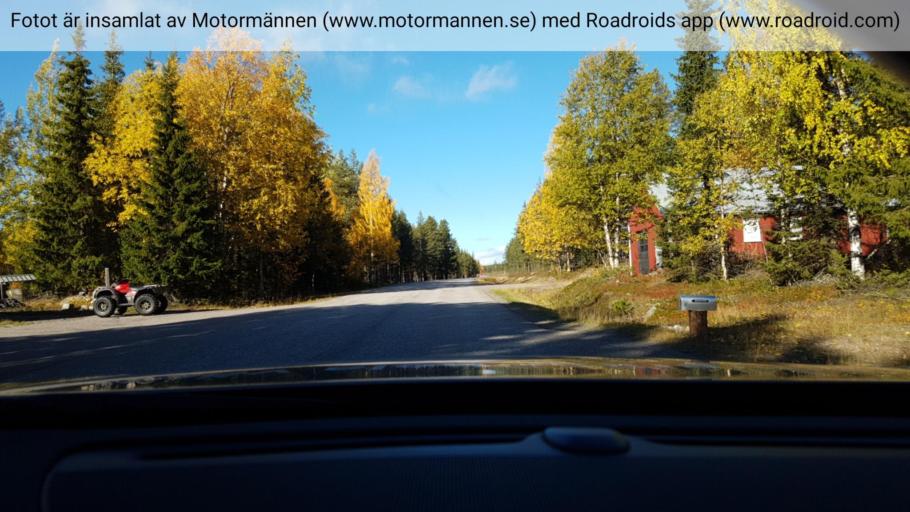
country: SE
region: Vaesterbotten
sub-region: Mala Kommun
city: Mala
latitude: 65.7675
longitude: 18.5435
